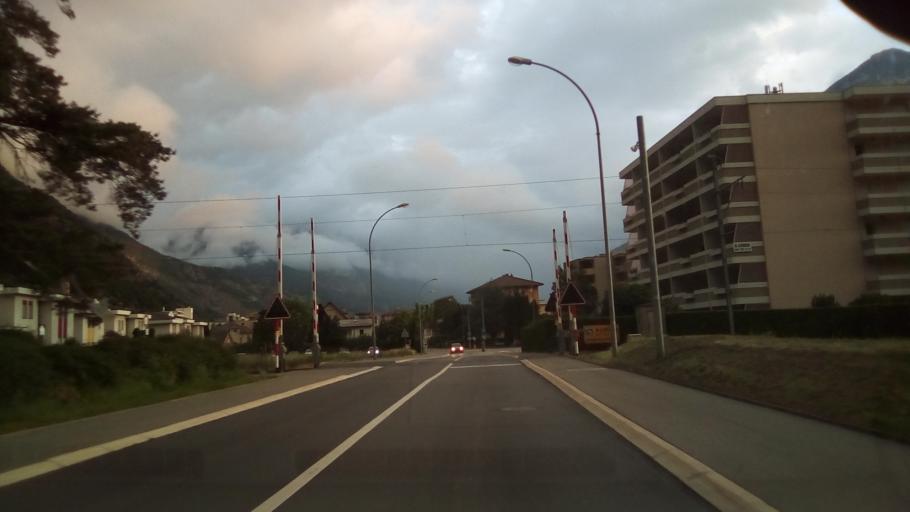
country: CH
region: Valais
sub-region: Martigny District
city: Martigny-Ville
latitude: 46.1009
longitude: 7.0818
